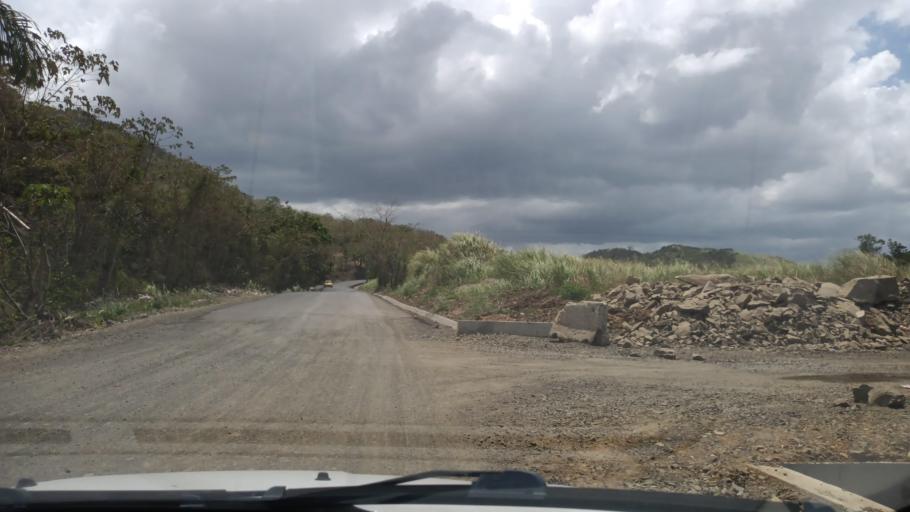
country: PA
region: Panama
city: Alcalde Diaz
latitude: 9.0916
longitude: -79.5775
